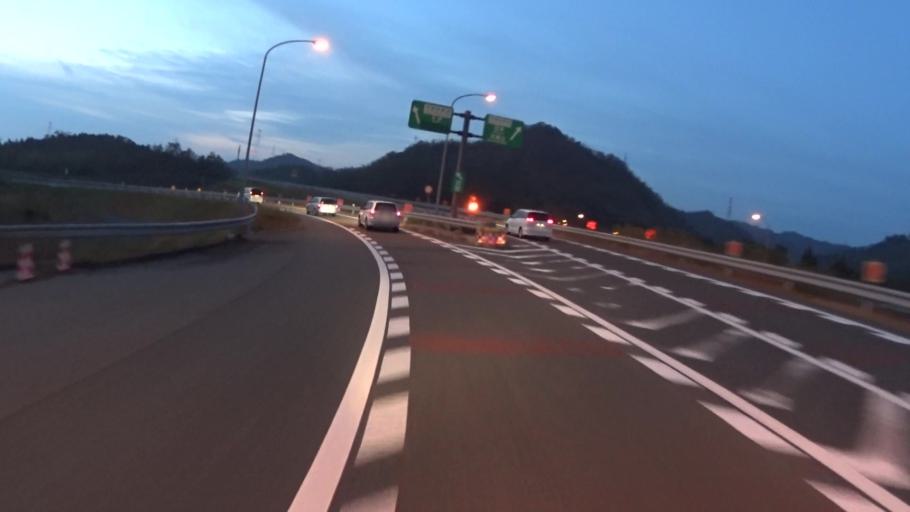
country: JP
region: Kyoto
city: Ayabe
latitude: 35.3550
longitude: 135.2911
